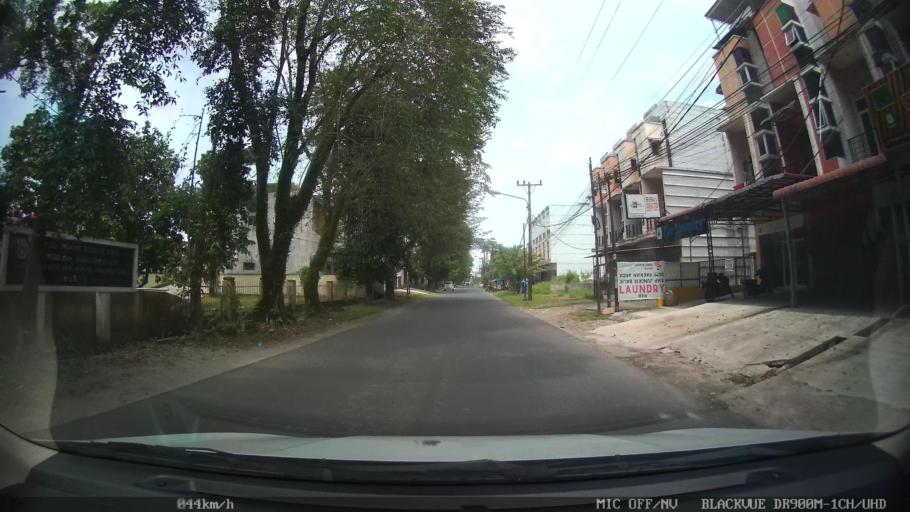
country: ID
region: North Sumatra
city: Sunggal
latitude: 3.5550
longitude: 98.6381
